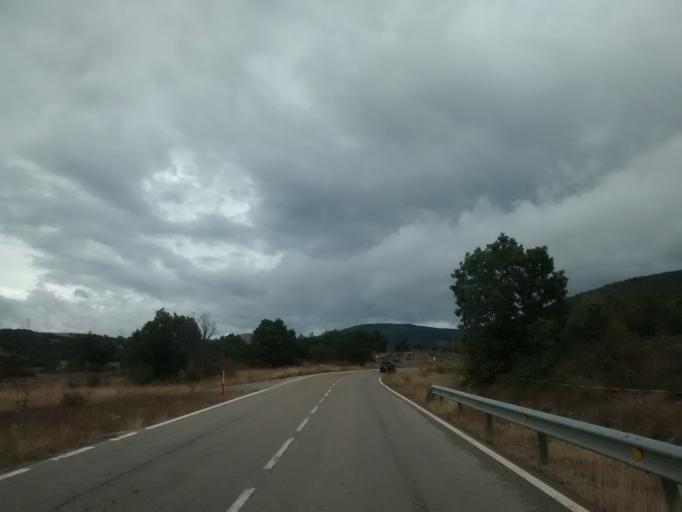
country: ES
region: Cantabria
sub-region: Provincia de Cantabria
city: Mataporquera
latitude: 42.8828
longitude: -4.0720
